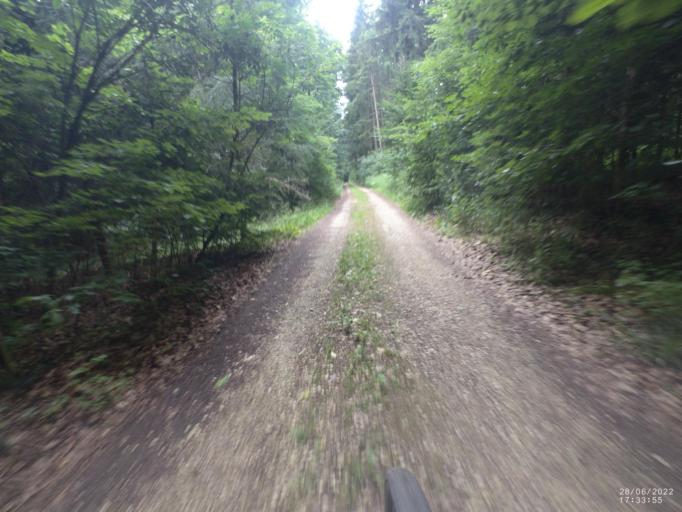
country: DE
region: Baden-Wuerttemberg
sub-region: Regierungsbezirk Stuttgart
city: Gerstetten
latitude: 48.6490
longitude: 10.0231
